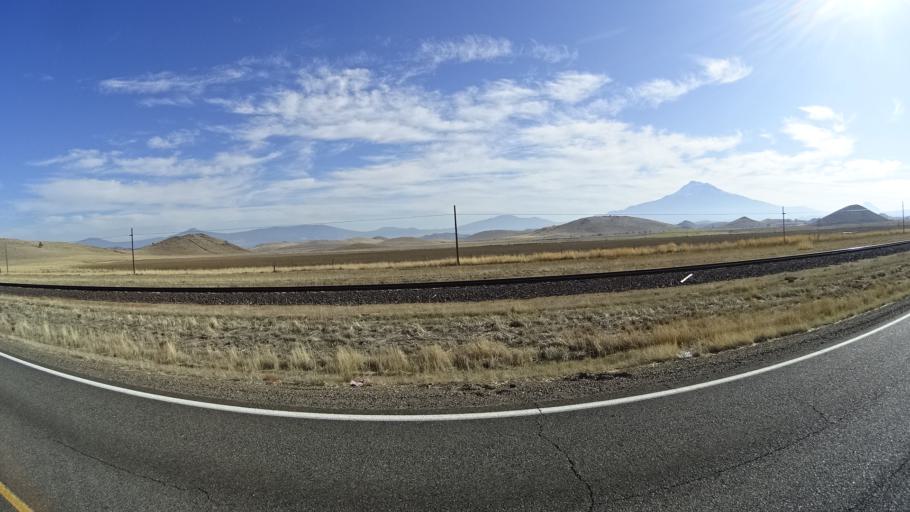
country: US
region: California
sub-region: Siskiyou County
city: Montague
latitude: 41.5494
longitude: -122.5262
